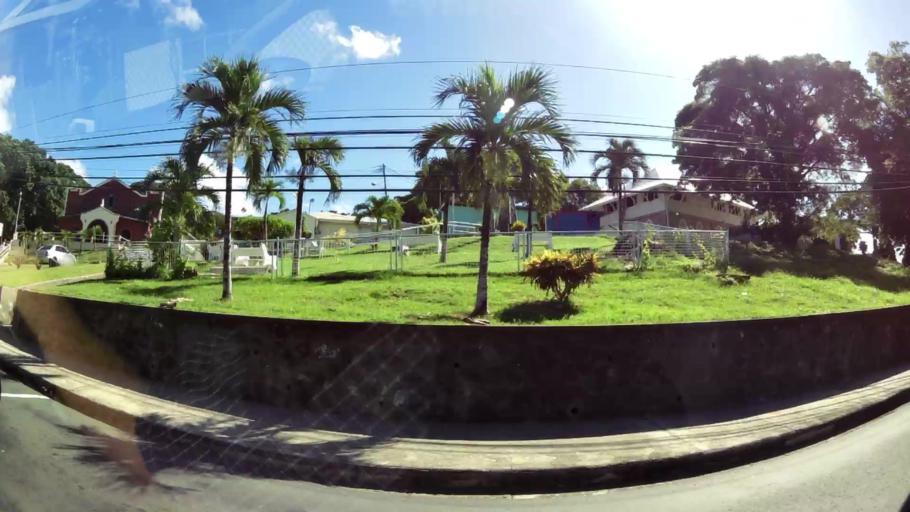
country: TT
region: Tobago
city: Scarborough
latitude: 11.1786
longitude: -60.7327
